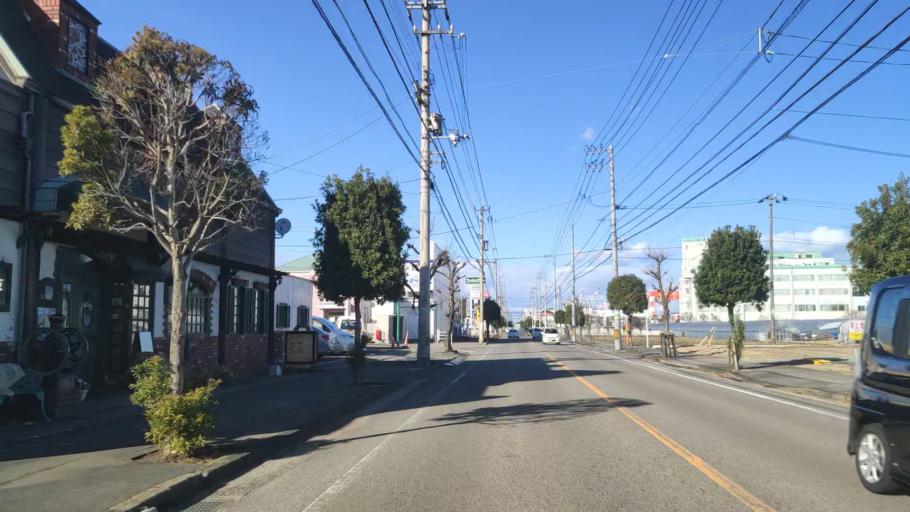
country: JP
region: Ehime
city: Saijo
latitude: 33.9270
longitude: 133.1907
